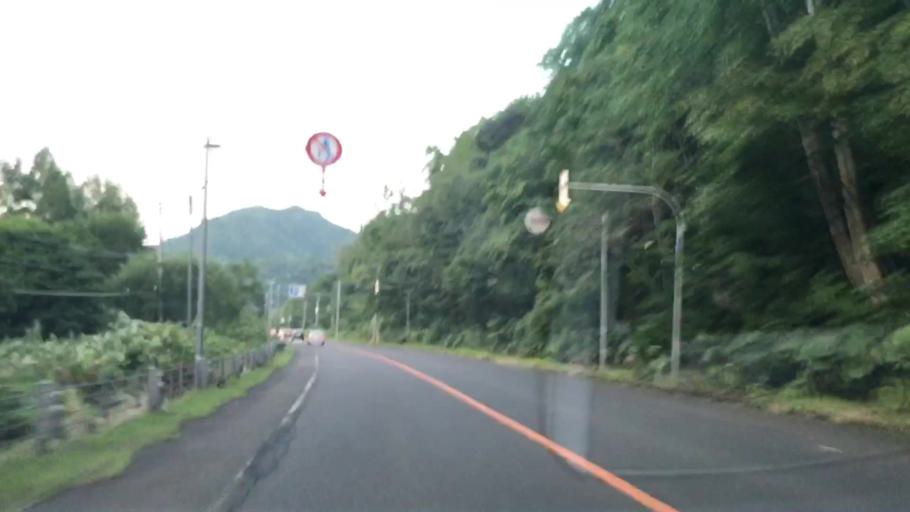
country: JP
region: Hokkaido
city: Sapporo
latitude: 42.9471
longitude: 141.1412
